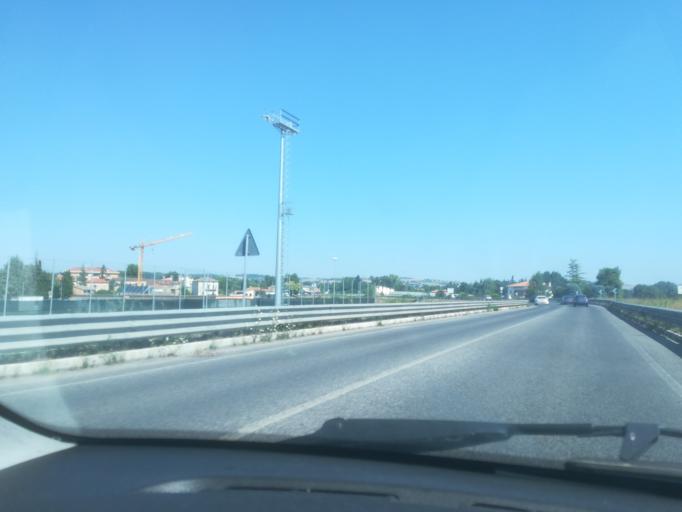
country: IT
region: The Marches
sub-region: Provincia di Macerata
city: Villa Potenza
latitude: 43.3233
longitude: 13.4294
